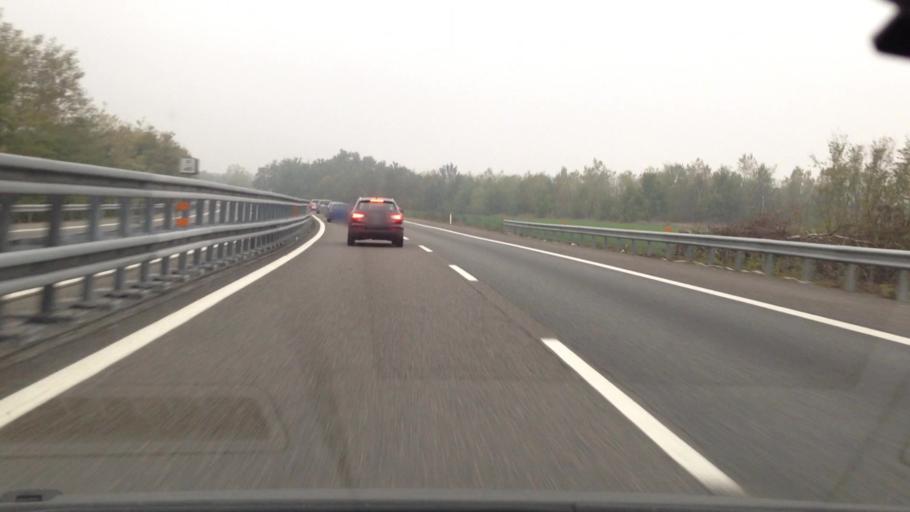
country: IT
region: Piedmont
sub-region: Provincia di Asti
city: Refrancore
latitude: 44.9091
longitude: 8.3323
